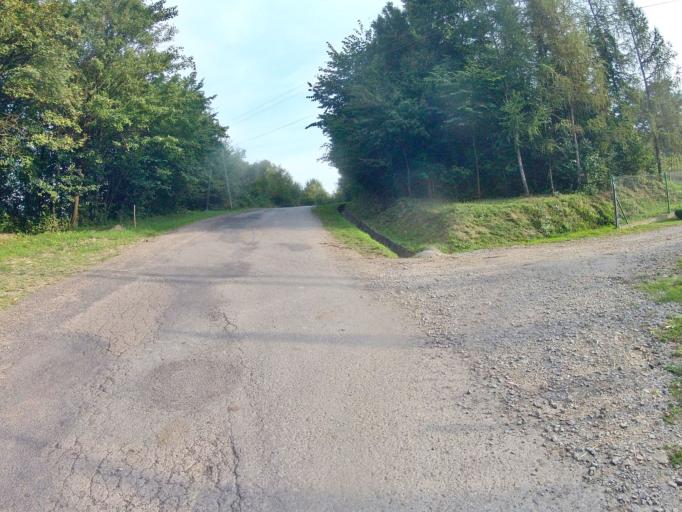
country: PL
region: Subcarpathian Voivodeship
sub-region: Powiat jasielski
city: Krempna
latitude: 49.5416
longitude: 21.5527
